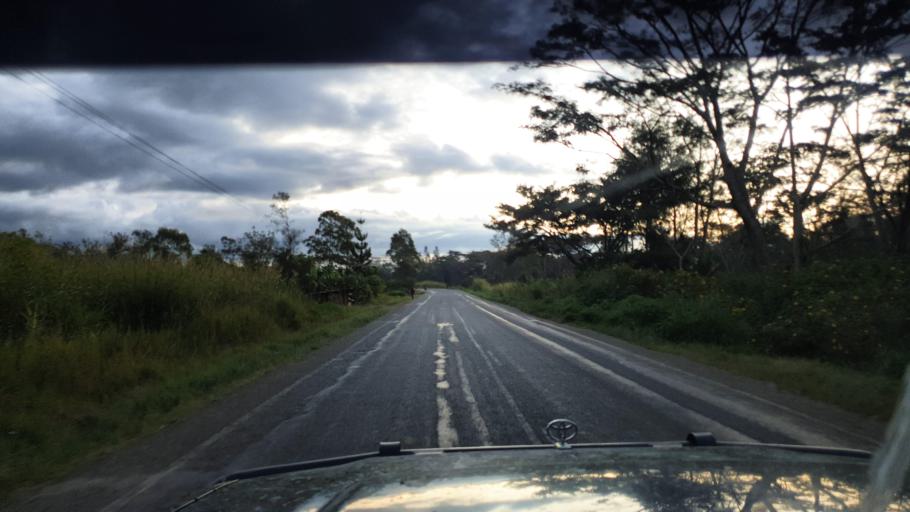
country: PG
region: Jiwaka
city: Minj
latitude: -5.8348
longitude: 144.5488
